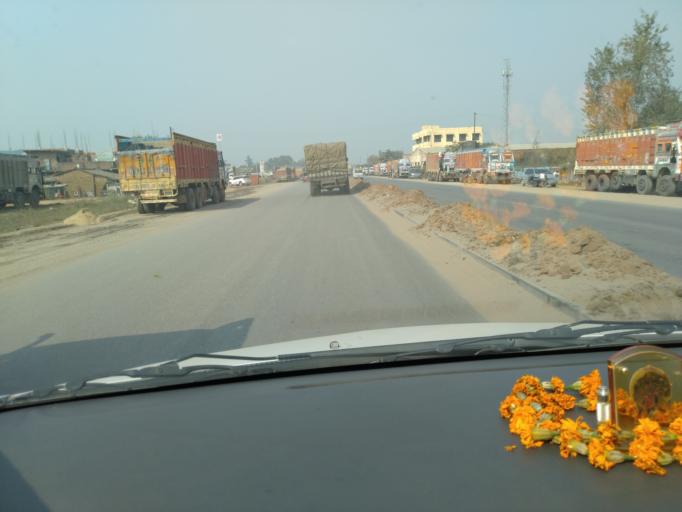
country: IN
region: Bihar
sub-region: Rohtas
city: Dehri
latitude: 24.9171
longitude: 84.1541
